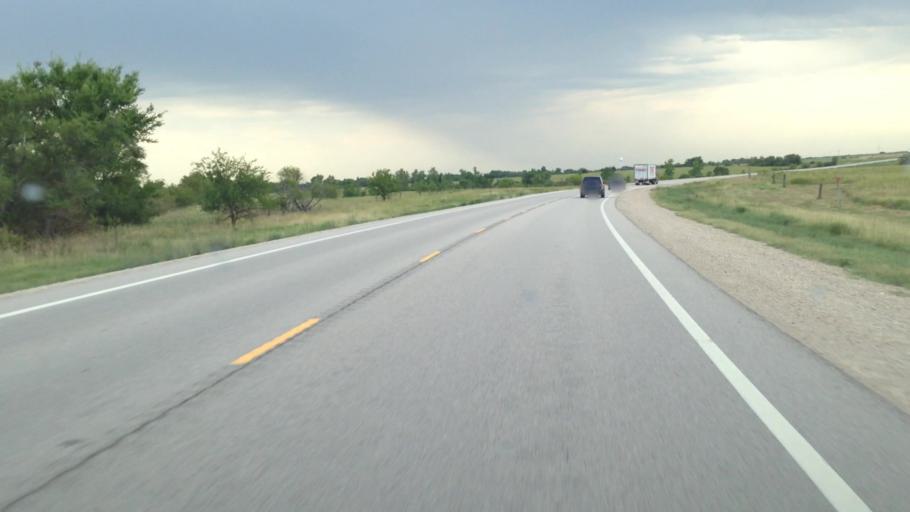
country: US
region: Kansas
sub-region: Coffey County
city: Burlington
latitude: 38.2983
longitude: -95.7290
